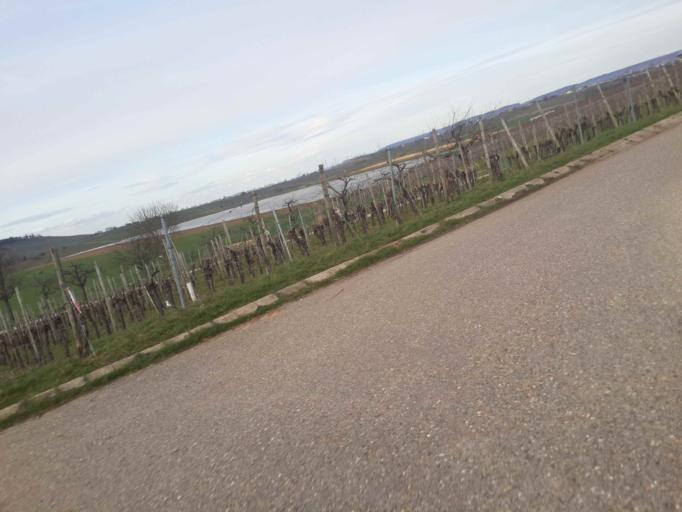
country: DE
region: Baden-Wuerttemberg
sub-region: Regierungsbezirk Stuttgart
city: Nordheim
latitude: 49.1052
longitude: 9.0943
